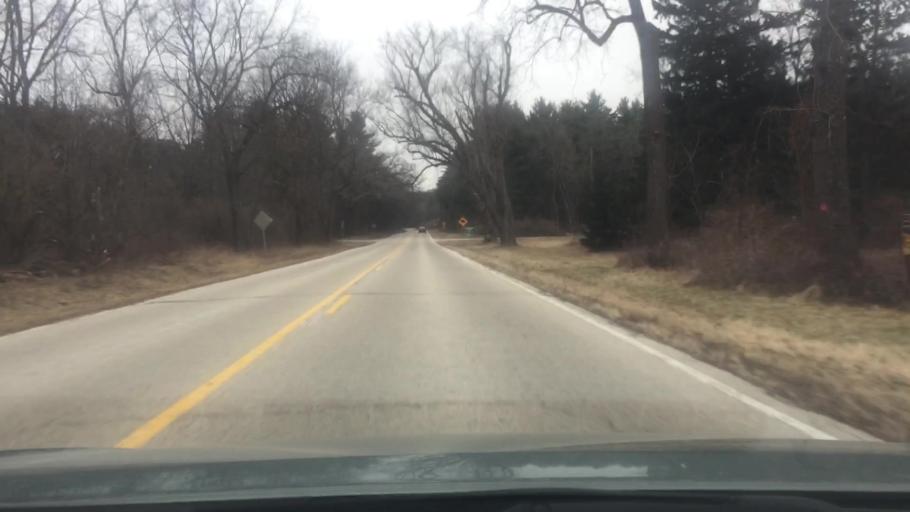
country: US
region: Wisconsin
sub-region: Waukesha County
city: North Prairie
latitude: 42.9385
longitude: -88.4623
